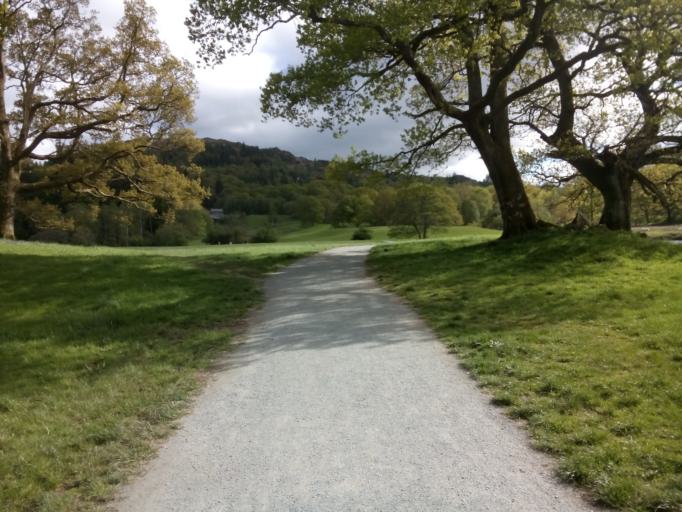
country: GB
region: England
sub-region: Cumbria
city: Ambleside
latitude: 54.4251
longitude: -3.0206
